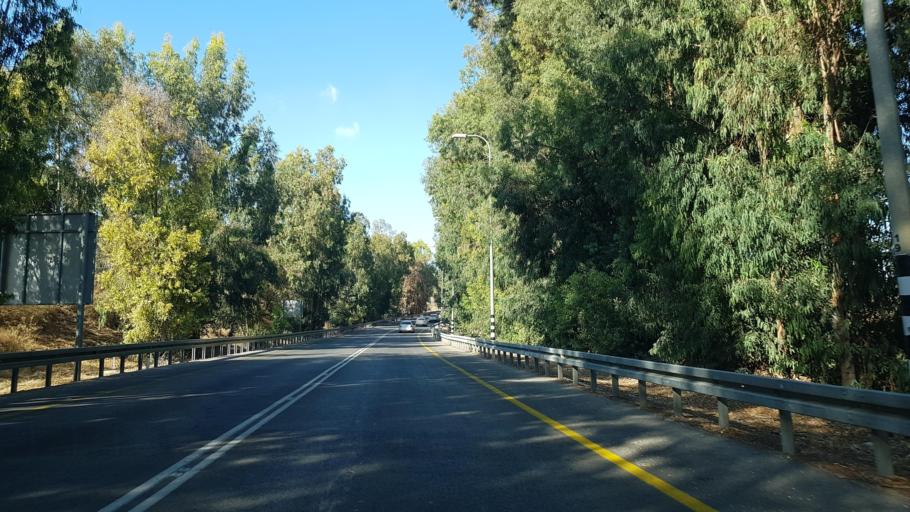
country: PS
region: West Bank
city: Tulkarm
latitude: 32.3531
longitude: 35.0143
